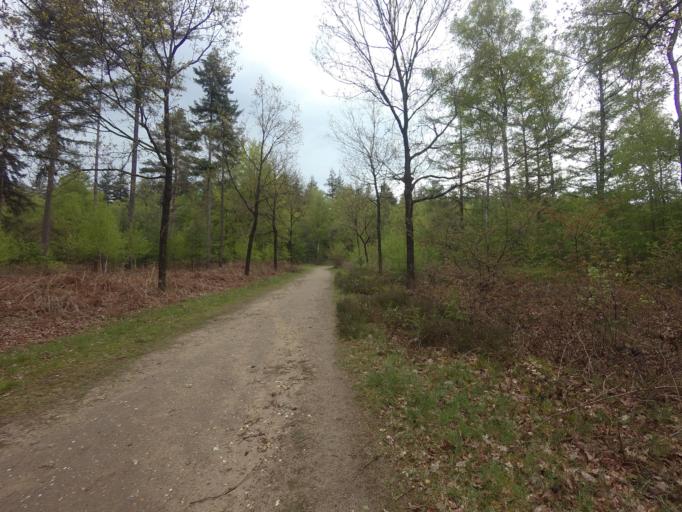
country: NL
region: Utrecht
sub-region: Gemeente Utrechtse Heuvelrug
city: Amerongen
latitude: 51.9978
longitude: 5.4846
